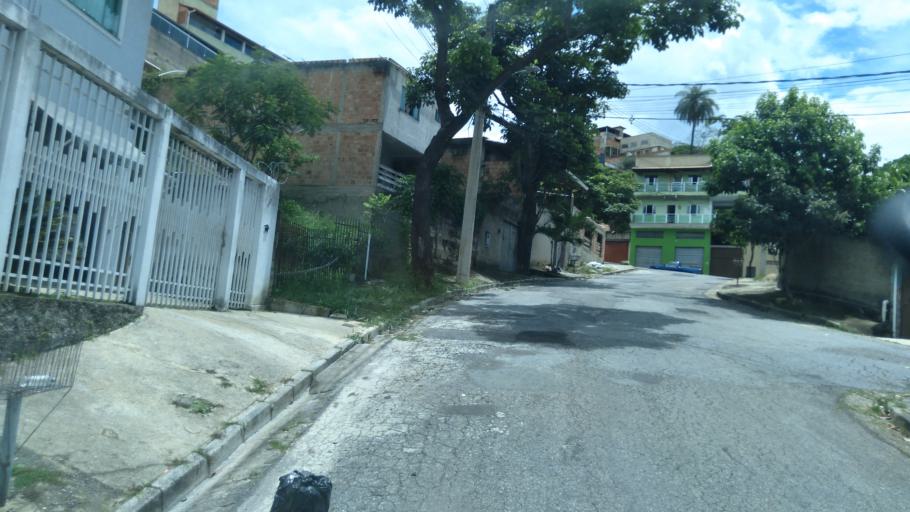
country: BR
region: Minas Gerais
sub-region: Belo Horizonte
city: Belo Horizonte
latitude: -19.8593
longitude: -43.8756
